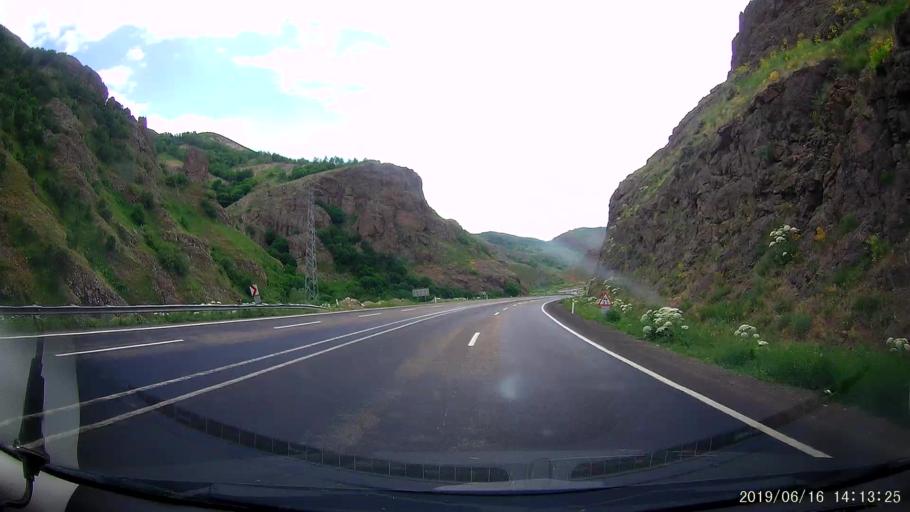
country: TR
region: Agri
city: Tahir
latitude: 39.7969
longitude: 42.5173
